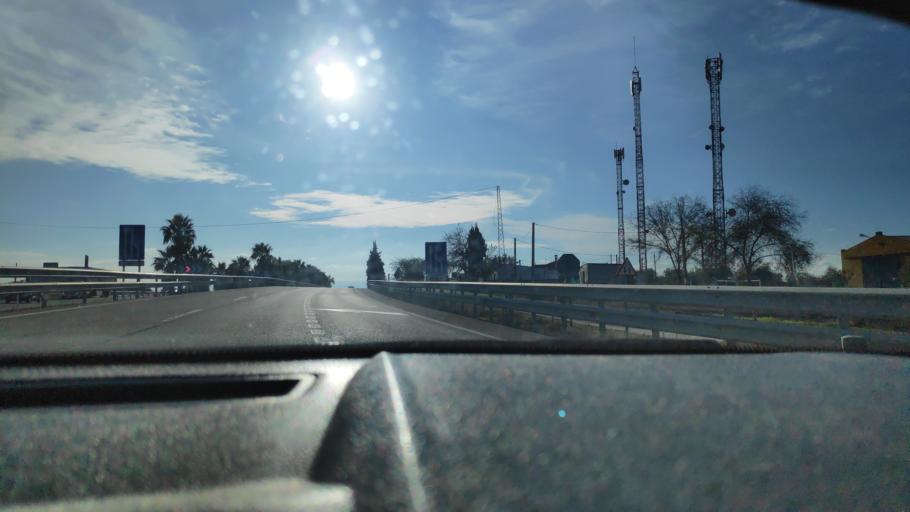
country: ES
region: Andalusia
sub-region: Province of Cordoba
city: La Carlota
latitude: 37.5919
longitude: -4.9799
